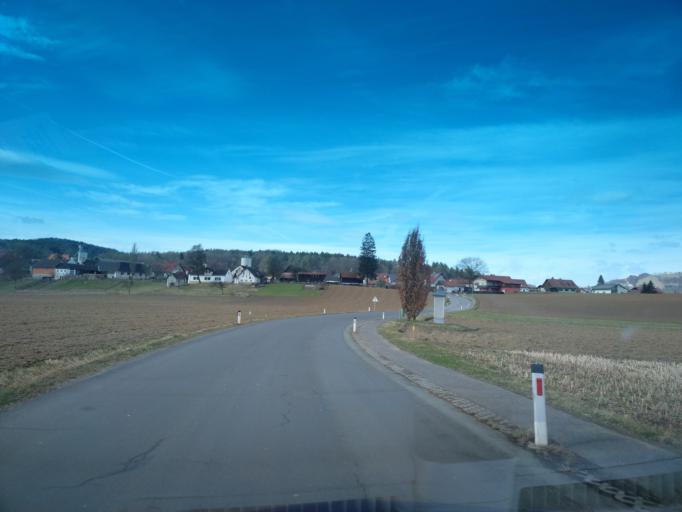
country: AT
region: Styria
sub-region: Politischer Bezirk Leibnitz
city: Grossklein
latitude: 46.7387
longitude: 15.4336
